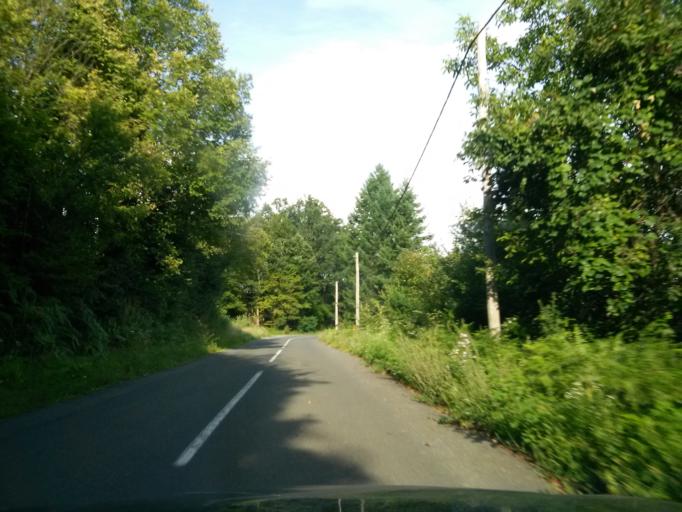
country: HR
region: Sisacko-Moslavacka
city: Gvozd
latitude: 45.4799
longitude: 15.8940
